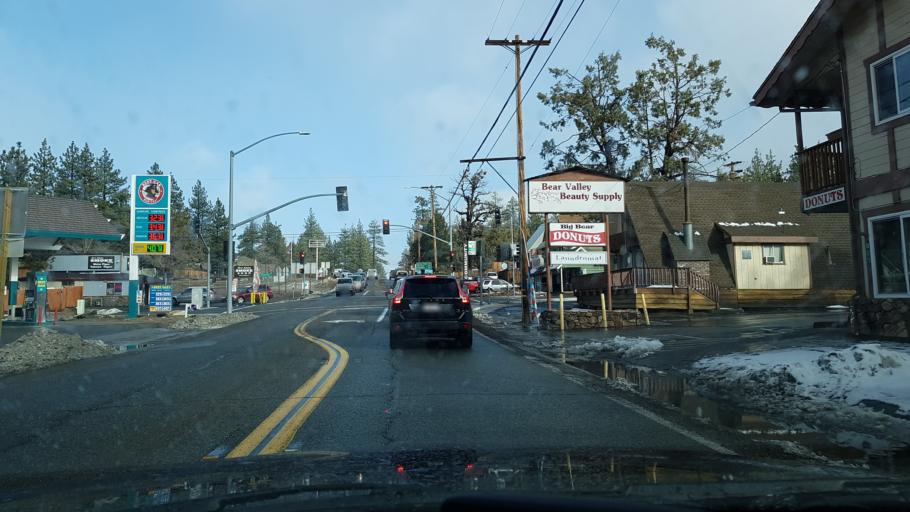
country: US
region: California
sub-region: San Bernardino County
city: Big Bear City
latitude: 34.2611
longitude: -116.8463
